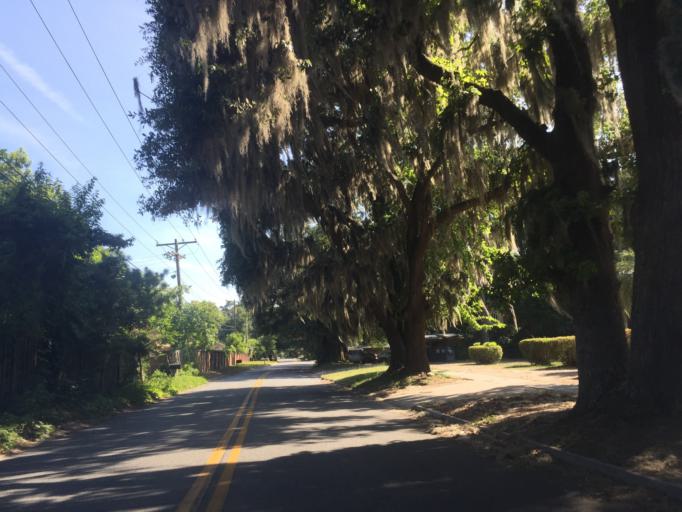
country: US
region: Georgia
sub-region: Chatham County
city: Isle of Hope
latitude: 31.9895
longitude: -81.0956
